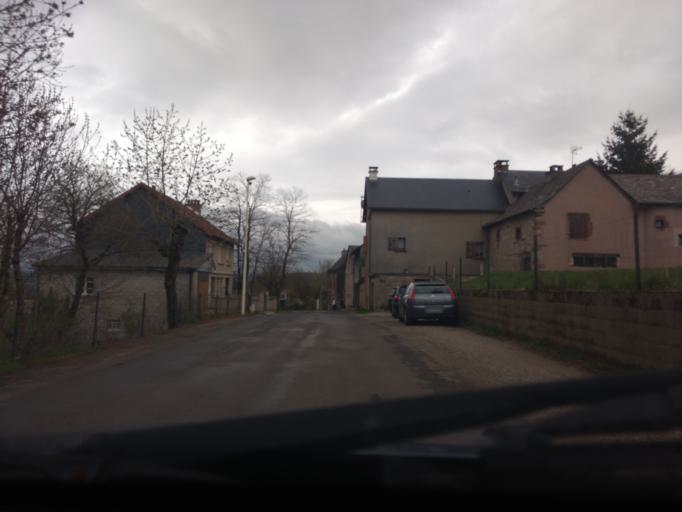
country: FR
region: Midi-Pyrenees
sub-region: Departement de l'Aveyron
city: La Loubiere
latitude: 44.3971
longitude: 2.7016
